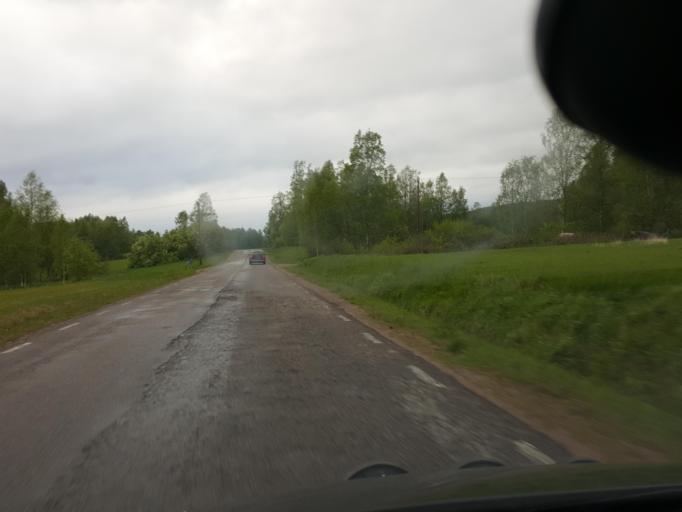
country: SE
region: Gaevleborg
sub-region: Ljusdals Kommun
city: Jaervsoe
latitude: 61.7904
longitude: 16.2144
